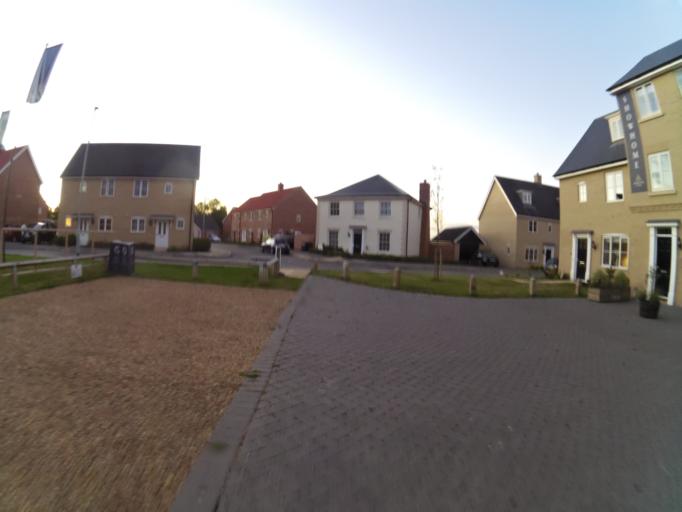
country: GB
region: England
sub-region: Suffolk
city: Bramford
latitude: 52.0804
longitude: 1.0943
